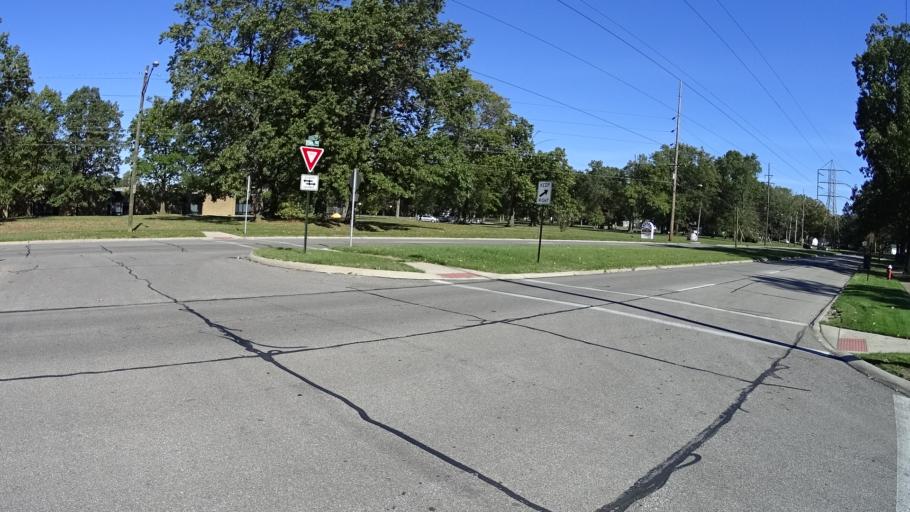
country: US
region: Ohio
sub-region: Lorain County
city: Lorain
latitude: 41.4363
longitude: -82.1764
